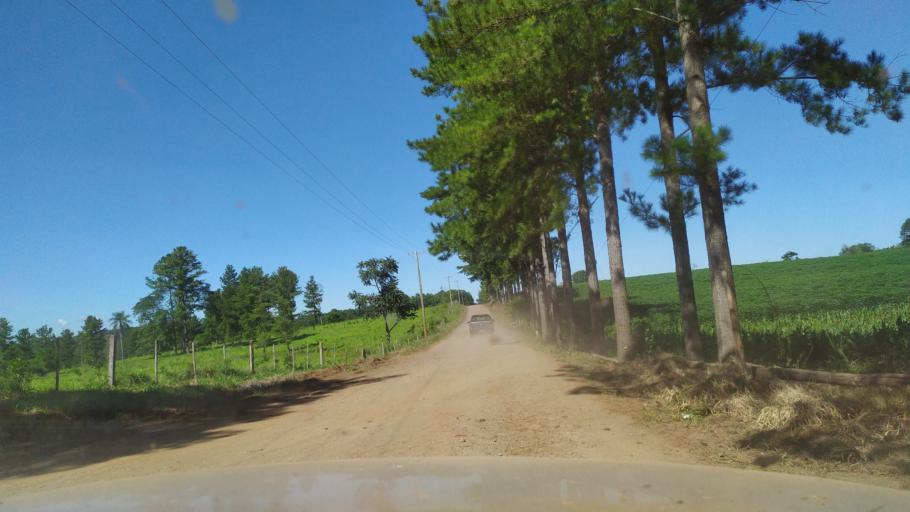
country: AR
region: Misiones
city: Caraguatay
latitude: -26.6788
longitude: -54.7050
